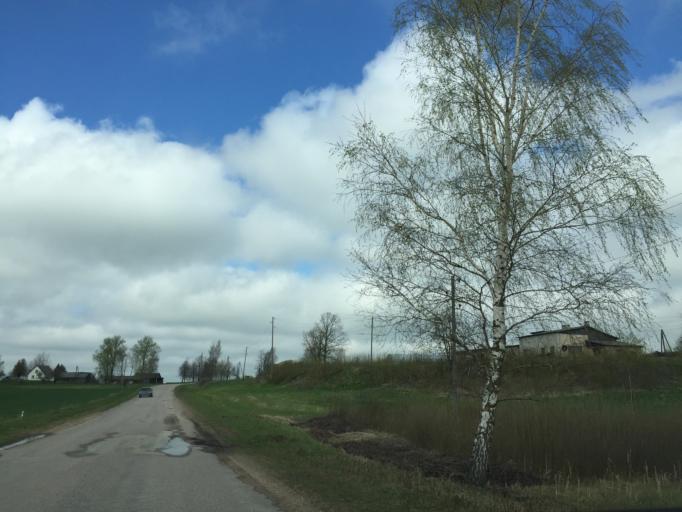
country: EE
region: Valgamaa
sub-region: Valga linn
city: Valga
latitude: 57.5488
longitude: 26.2922
